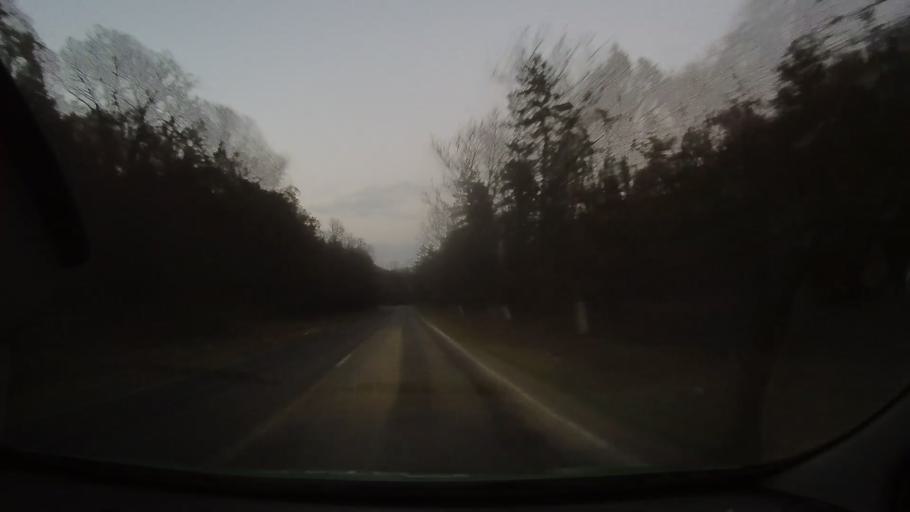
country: RO
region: Constanta
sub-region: Comuna Baneasa
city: Baneasa
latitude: 44.0790
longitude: 27.7388
